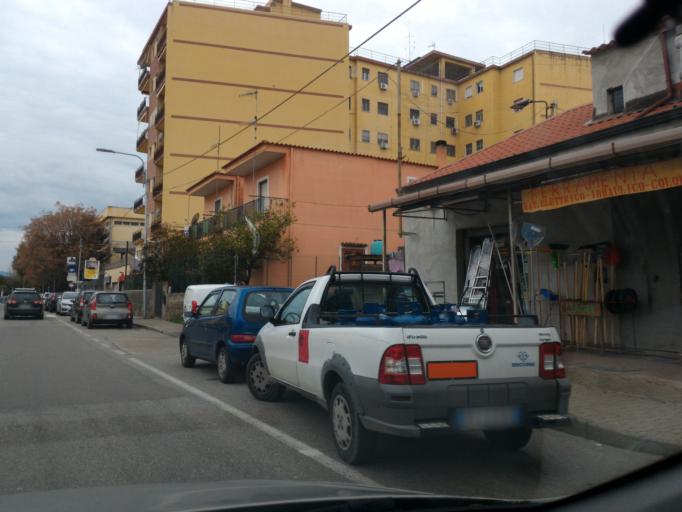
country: IT
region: Calabria
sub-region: Provincia di Catanzaro
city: Barone
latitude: 38.8287
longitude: 16.6235
